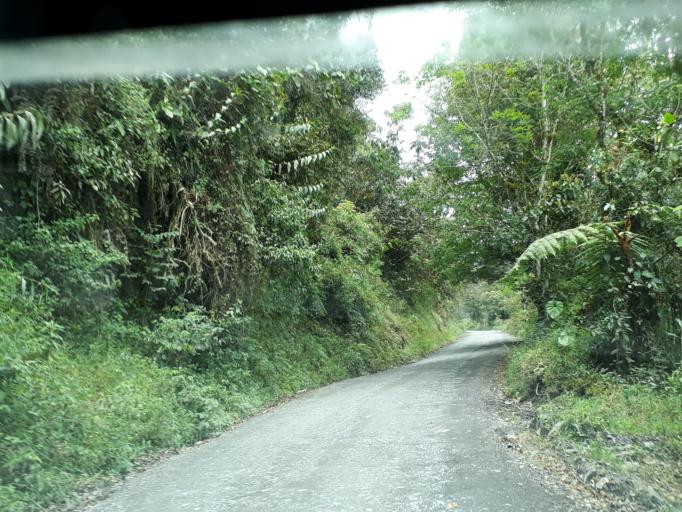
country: CO
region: Cundinamarca
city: Pacho
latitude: 5.2590
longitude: -74.1803
